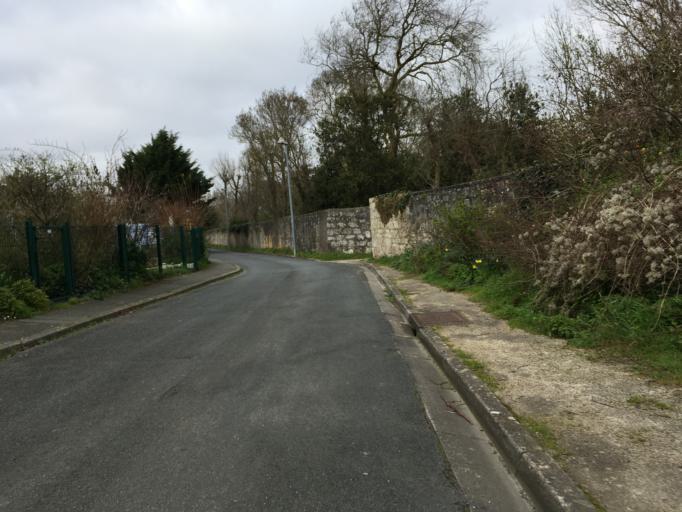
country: FR
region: Poitou-Charentes
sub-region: Departement de la Charente-Maritime
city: La Rochelle
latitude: 46.1770
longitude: -1.1449
